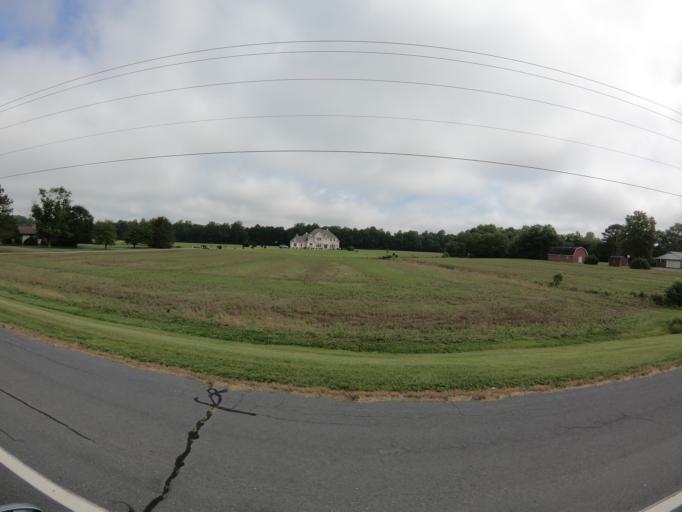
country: US
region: Delaware
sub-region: Kent County
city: Riverview
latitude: 39.0054
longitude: -75.5395
